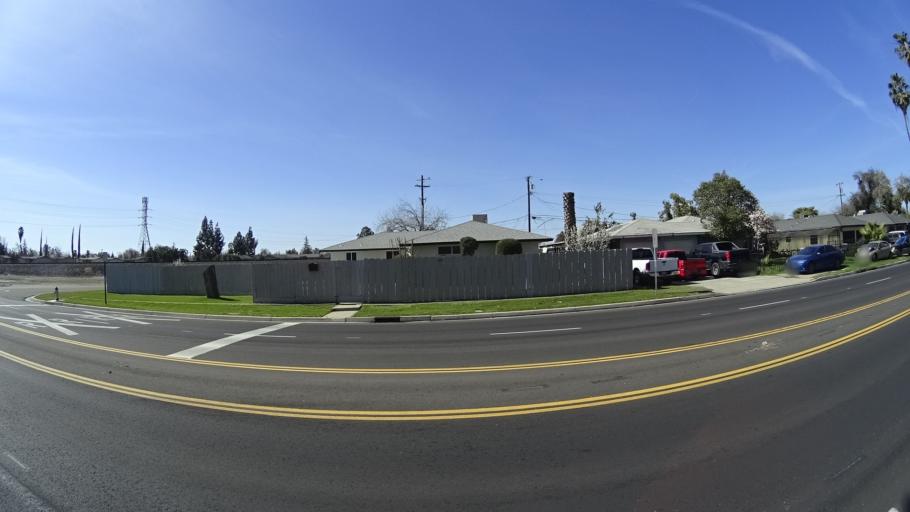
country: US
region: California
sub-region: Fresno County
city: Fresno
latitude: 36.7877
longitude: -119.8086
